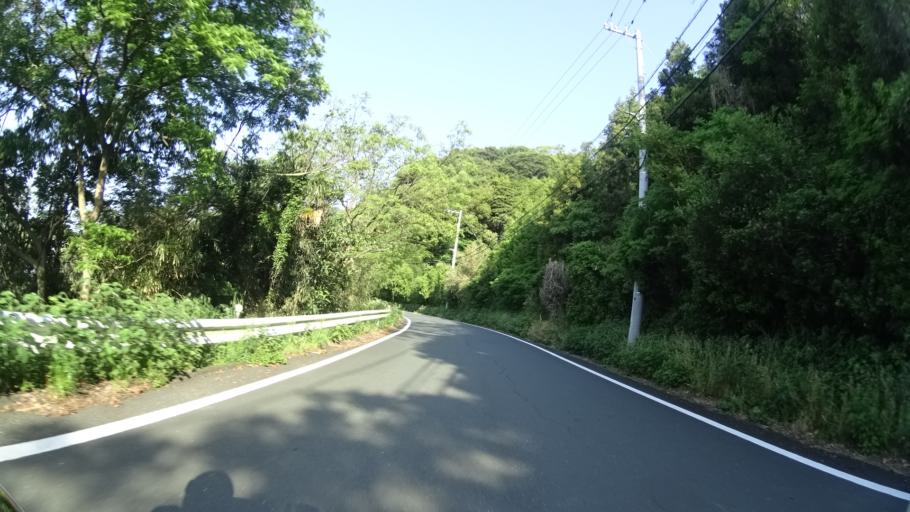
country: JP
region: Ehime
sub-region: Nishiuwa-gun
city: Ikata-cho
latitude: 33.3890
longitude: 132.0969
